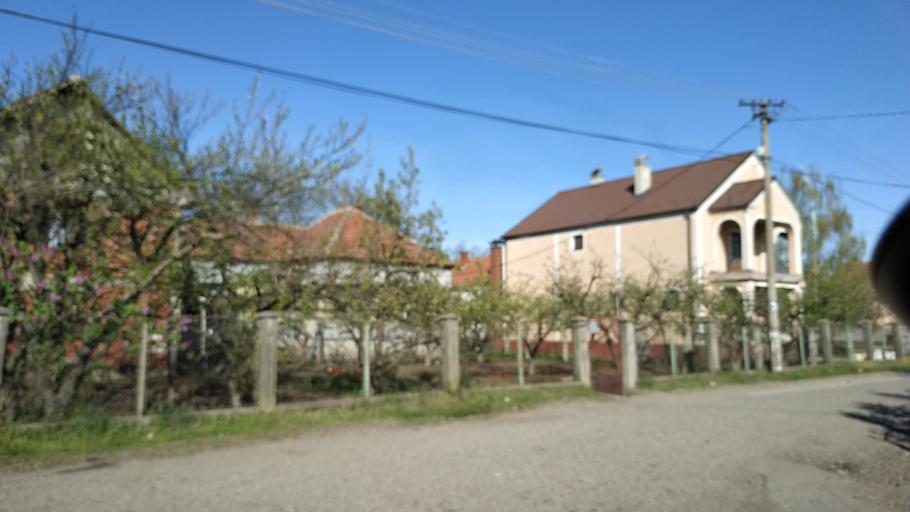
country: RS
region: Central Serbia
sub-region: Nisavski Okrug
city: Aleksinac
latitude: 43.5120
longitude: 21.6933
